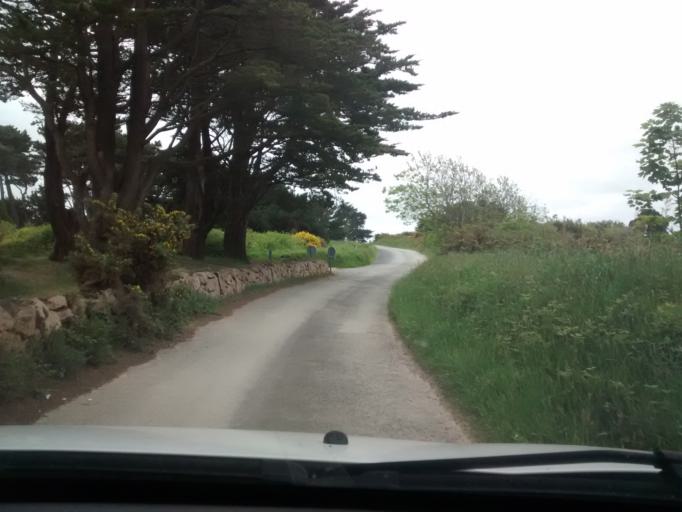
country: FR
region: Brittany
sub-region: Departement des Cotes-d'Armor
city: Tregastel
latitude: 48.8352
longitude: -3.4805
